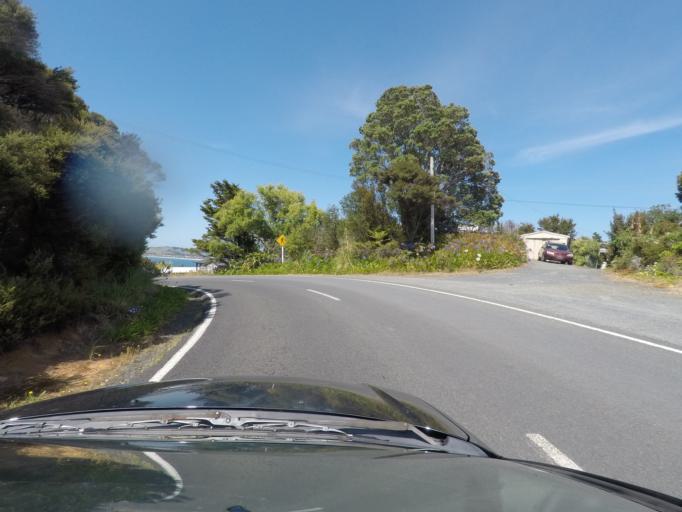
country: NZ
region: Auckland
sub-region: Auckland
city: Warkworth
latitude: -36.3129
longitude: 174.7909
